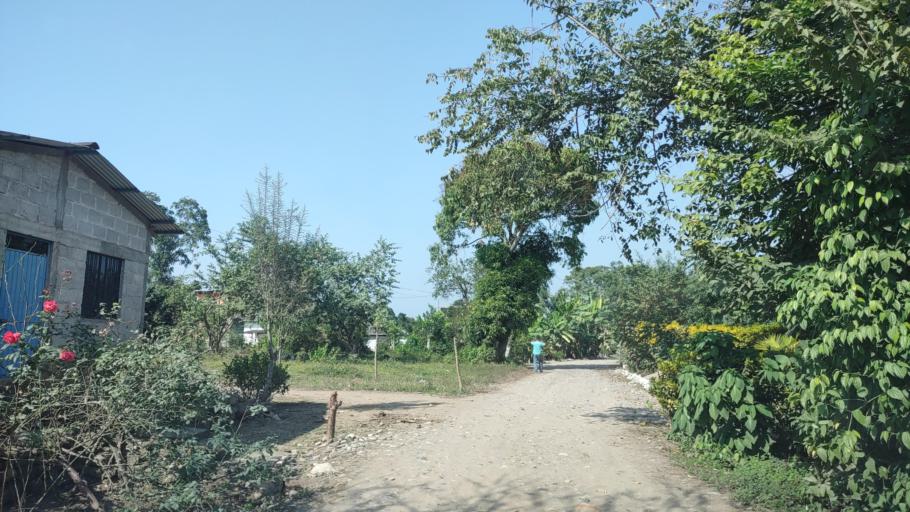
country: MX
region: Veracruz
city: Agua Dulce
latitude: 20.2770
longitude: -97.2857
